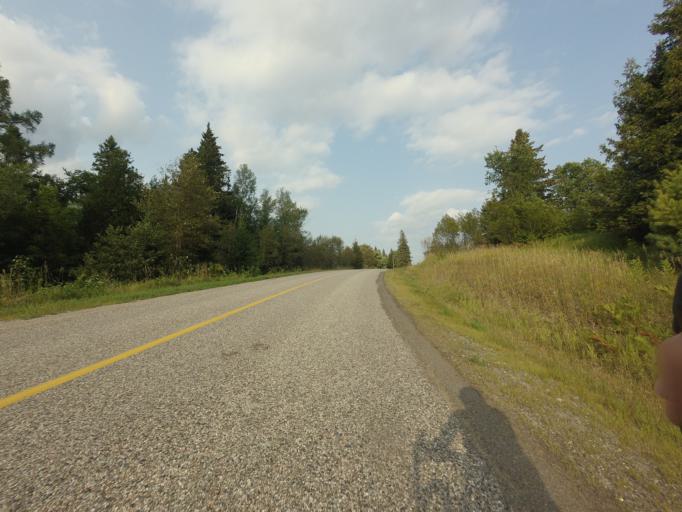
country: CA
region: Ontario
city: Perth
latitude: 44.8730
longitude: -76.7100
